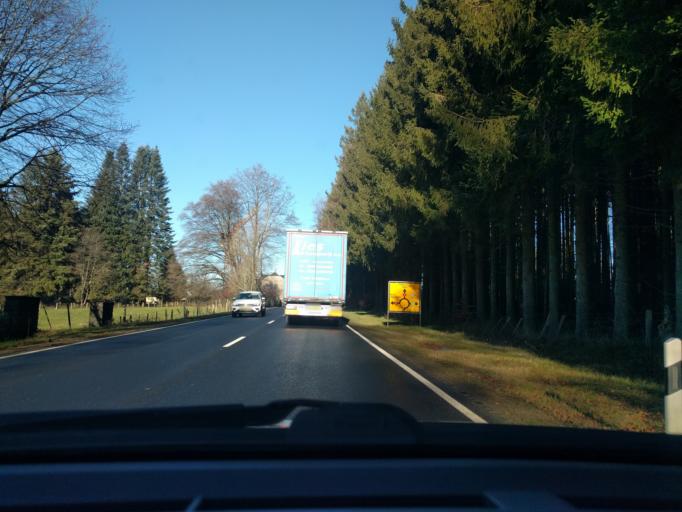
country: LU
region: Diekirch
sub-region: Canton de Clervaux
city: Weiswampach
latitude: 50.1530
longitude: 6.0531
